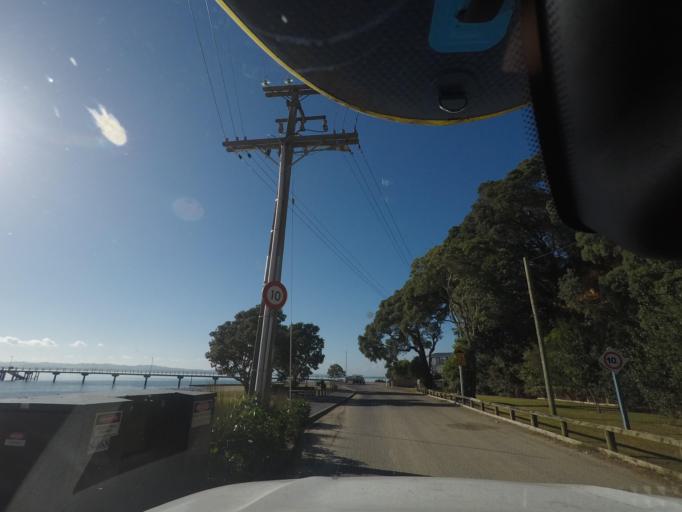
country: NZ
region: Auckland
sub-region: Auckland
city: Parakai
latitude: -36.5699
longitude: 174.3787
